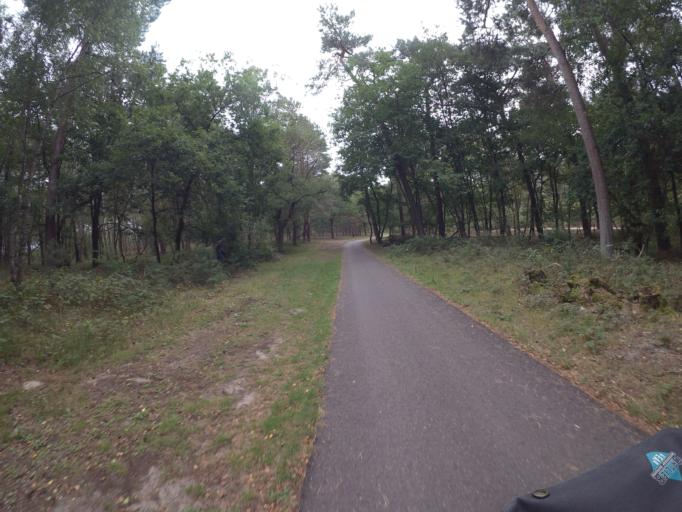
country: NL
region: North Brabant
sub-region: Gemeente Oss
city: Berghem
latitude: 51.7587
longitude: 5.5928
